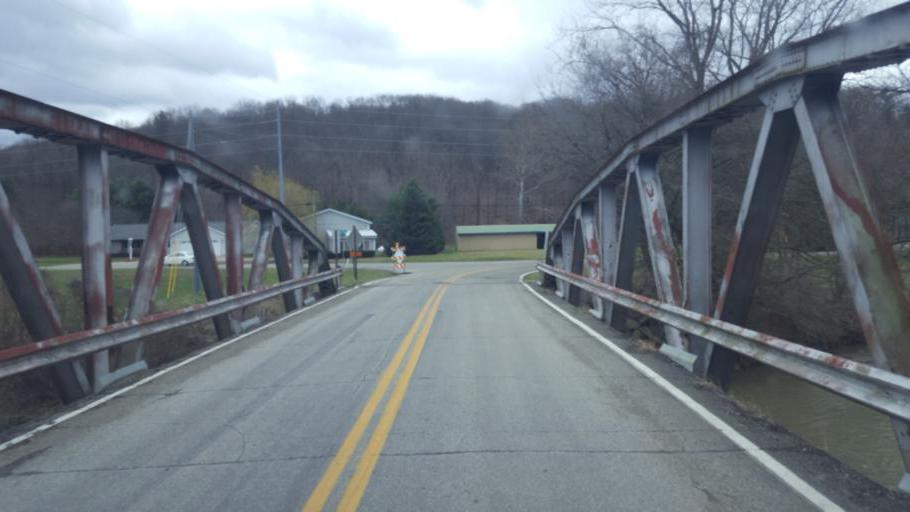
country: US
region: Ohio
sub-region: Licking County
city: Newark
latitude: 40.1652
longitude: -82.2927
